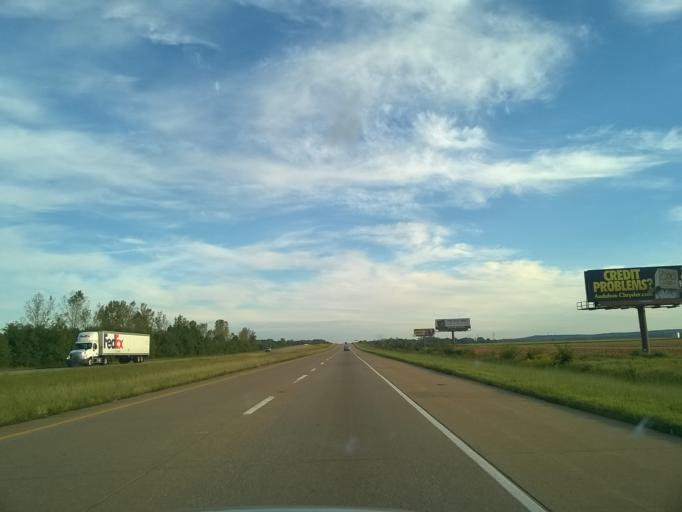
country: US
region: Indiana
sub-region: Vanderburgh County
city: Melody Hill
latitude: 38.0473
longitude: -87.4742
